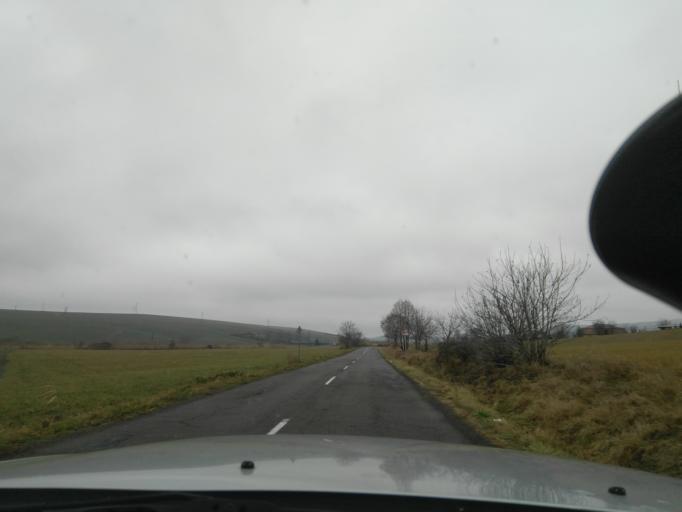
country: HU
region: Nograd
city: Kazar
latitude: 48.0407
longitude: 19.8749
